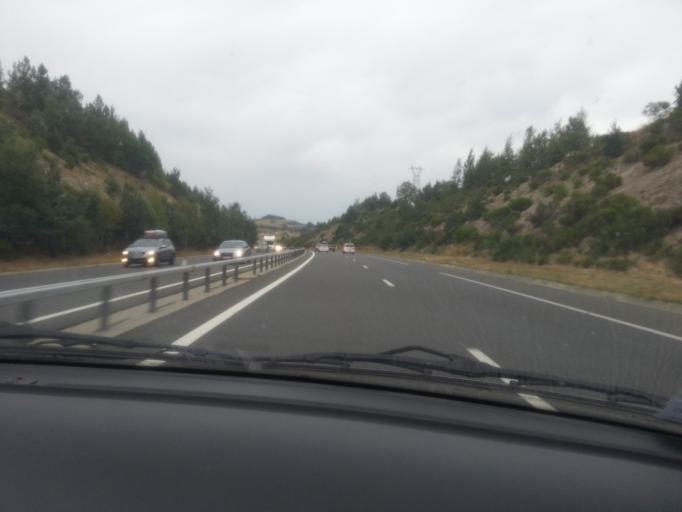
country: FR
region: Languedoc-Roussillon
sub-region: Departement de la Lozere
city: Marvejols
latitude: 44.6084
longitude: 3.2580
